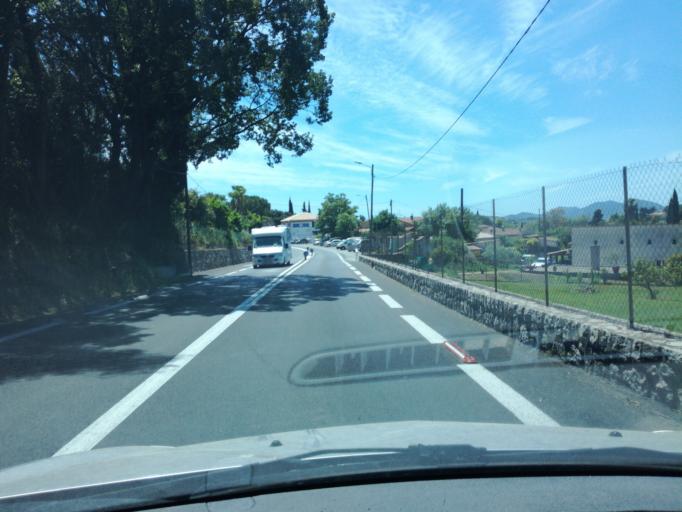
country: FR
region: Provence-Alpes-Cote d'Azur
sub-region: Departement des Alpes-Maritimes
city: Mougins
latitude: 43.5943
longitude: 7.0016
